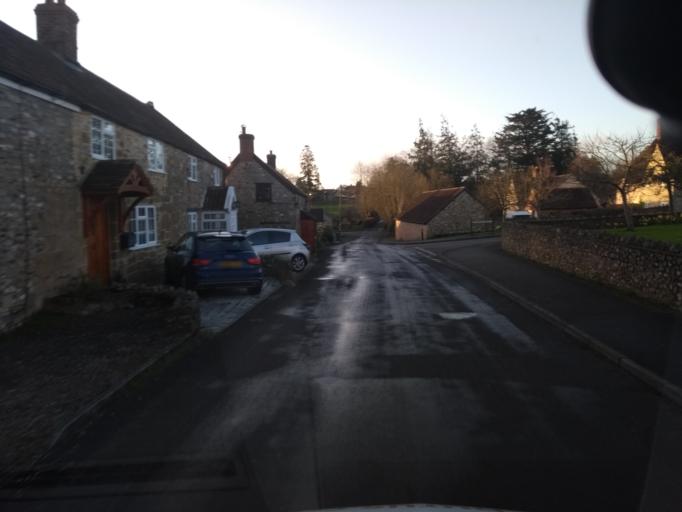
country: GB
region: England
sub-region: Somerset
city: Ilminster
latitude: 50.9336
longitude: -2.9683
